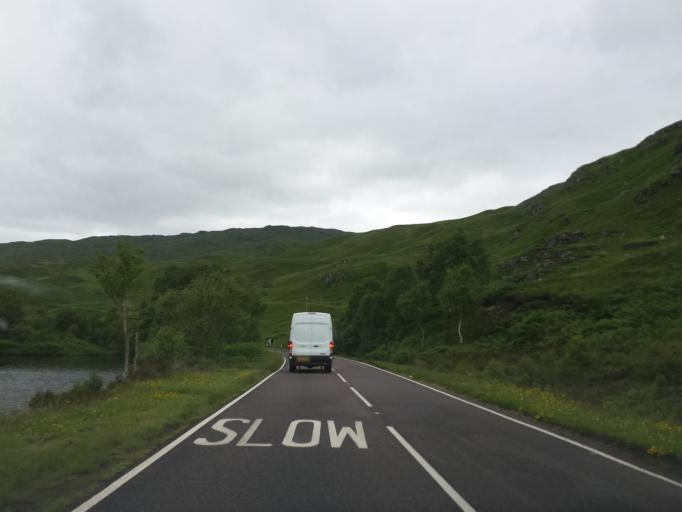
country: GB
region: Scotland
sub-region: Argyll and Bute
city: Isle Of Mull
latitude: 56.8842
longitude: -5.6145
